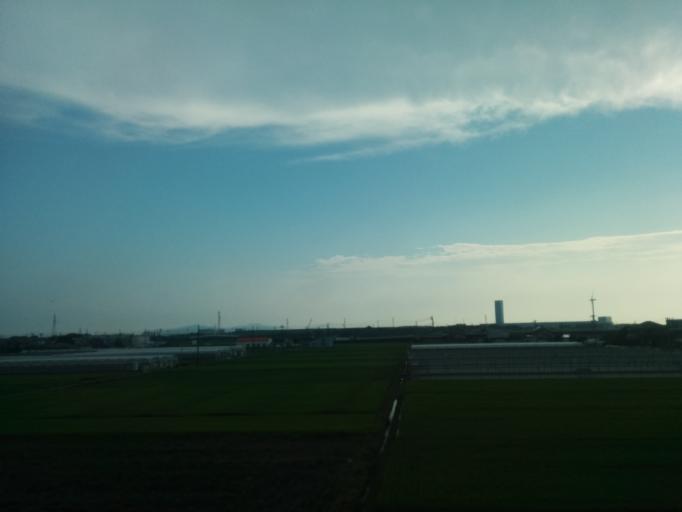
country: JP
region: Aichi
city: Kozakai-cho
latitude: 34.8005
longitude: 137.3226
